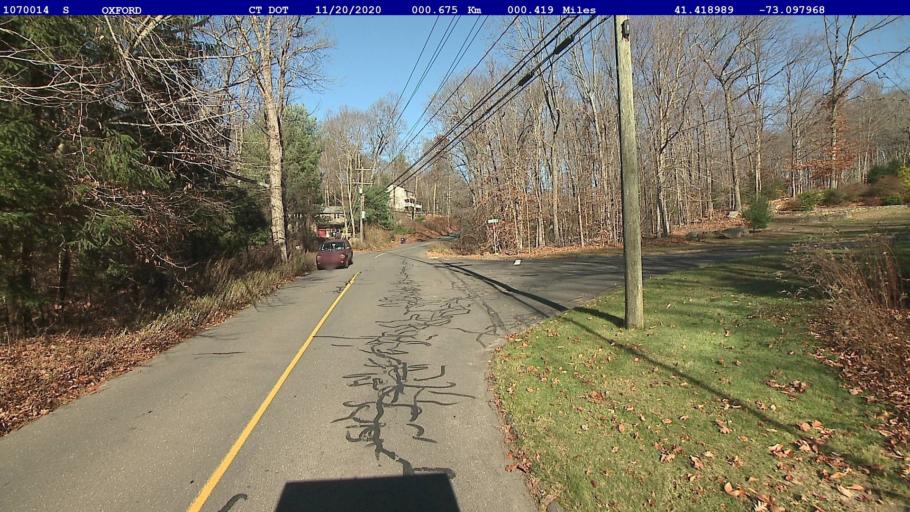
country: US
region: Connecticut
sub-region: New Haven County
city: Oxford
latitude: 41.4190
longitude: -73.0980
